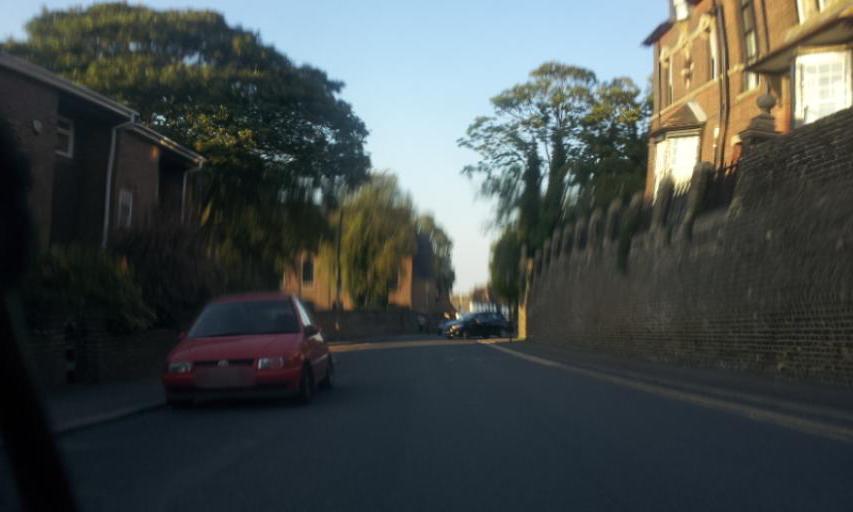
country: GB
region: England
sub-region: Medway
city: Rochester
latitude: 51.3840
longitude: 0.4989
